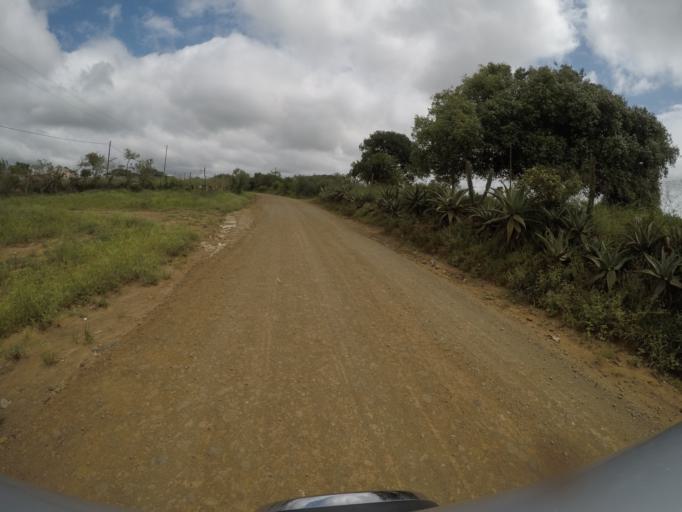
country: ZA
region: KwaZulu-Natal
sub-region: uThungulu District Municipality
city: Empangeni
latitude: -28.5778
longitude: 31.8468
